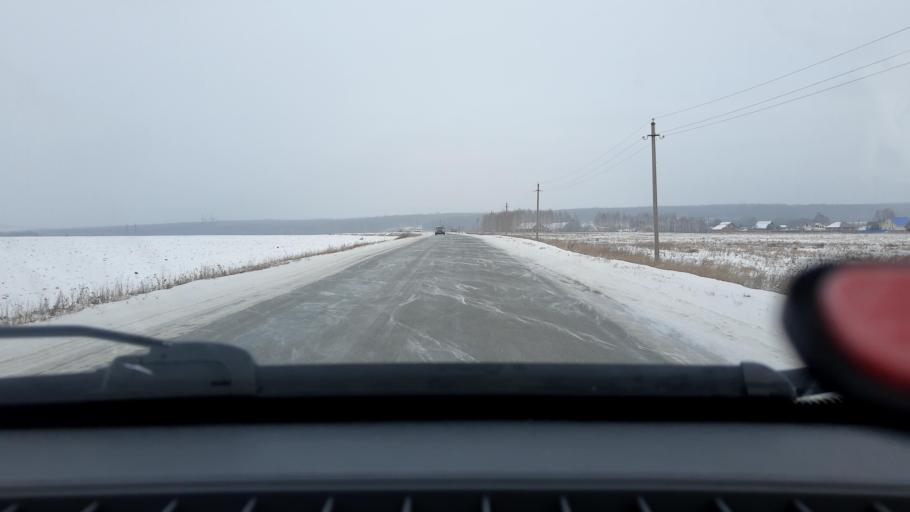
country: RU
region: Bashkortostan
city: Iglino
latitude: 54.7490
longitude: 56.3993
